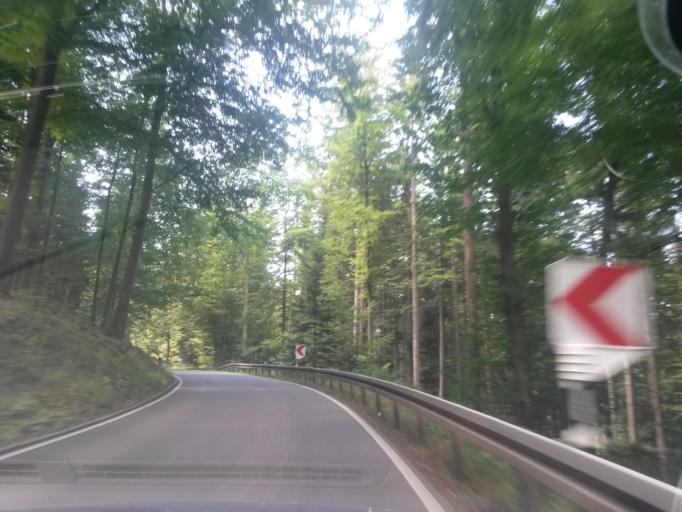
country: DE
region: Baden-Wuerttemberg
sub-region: Karlsruhe Region
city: Neuenburg
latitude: 48.8320
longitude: 8.5723
